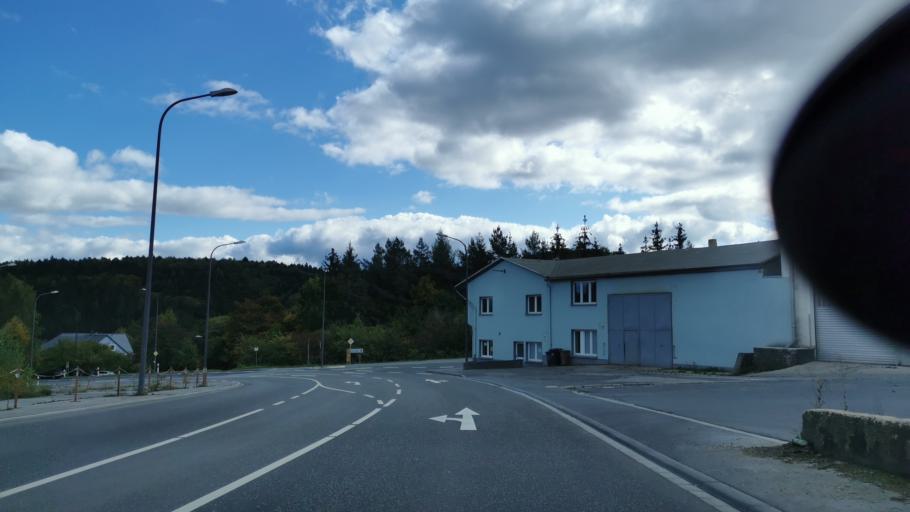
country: DE
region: Rheinland-Pfalz
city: Nohn
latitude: 50.3371
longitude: 6.7661
